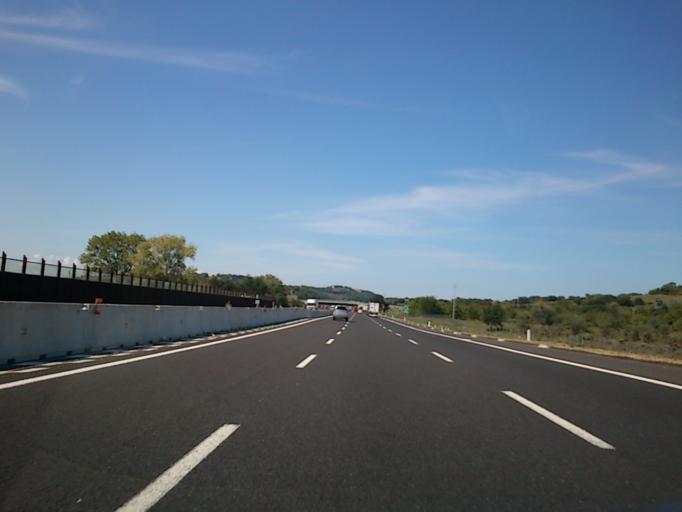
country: IT
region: The Marches
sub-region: Provincia di Pesaro e Urbino
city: Centinarola
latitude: 43.8376
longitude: 12.9893
